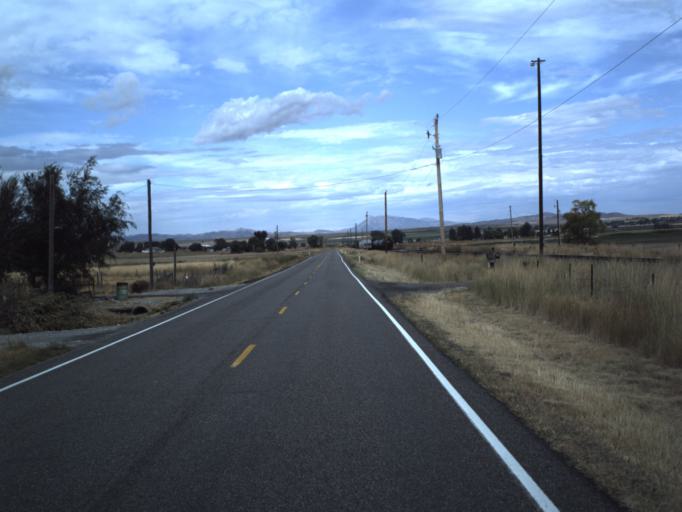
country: US
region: Utah
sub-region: Cache County
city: Benson
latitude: 41.8230
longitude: -111.9991
